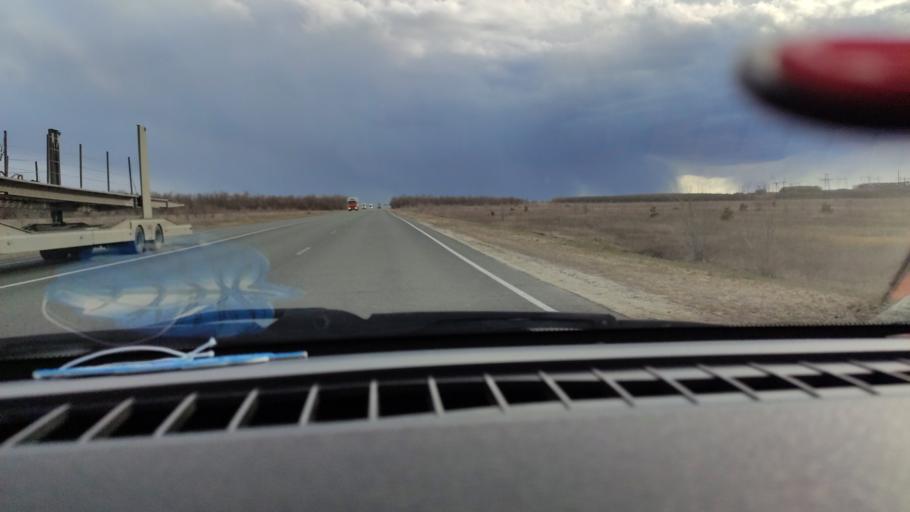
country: RU
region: Saratov
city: Sinodskoye
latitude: 51.9116
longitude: 46.5538
